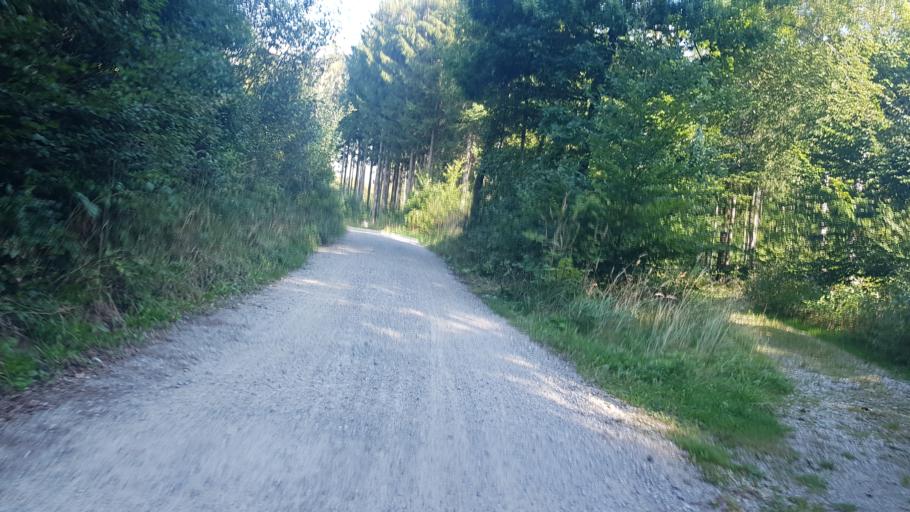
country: DE
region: Bavaria
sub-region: Upper Bavaria
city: Gilching
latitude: 48.0785
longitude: 11.3134
